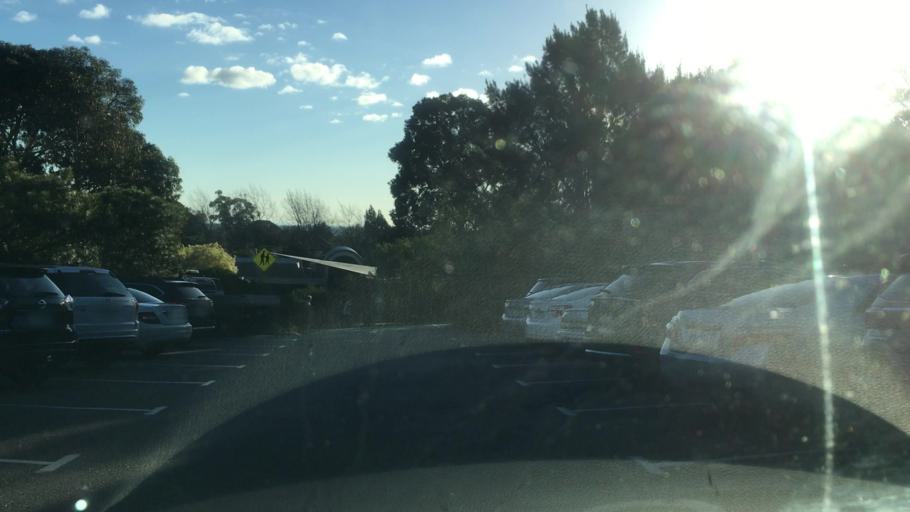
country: AU
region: Victoria
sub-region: Casey
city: Berwick
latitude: -38.0280
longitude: 145.3378
